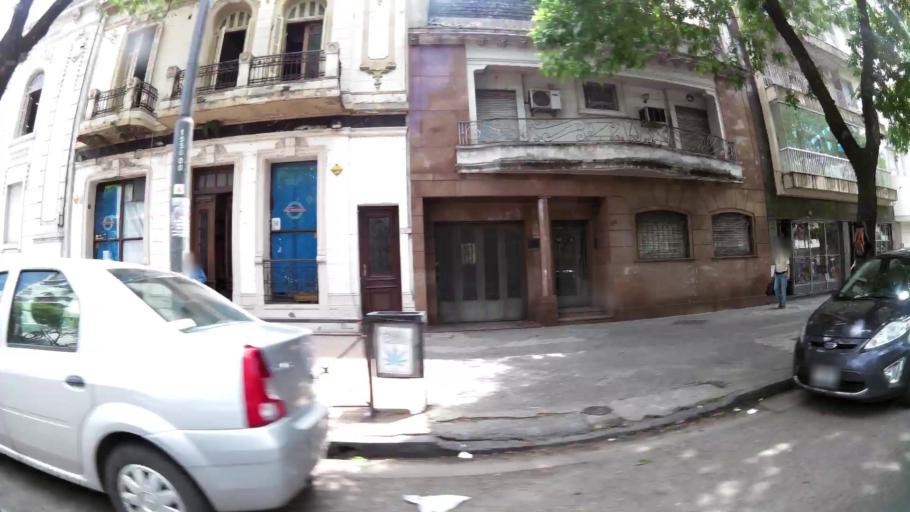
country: AR
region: Santa Fe
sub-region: Departamento de Rosario
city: Rosario
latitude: -32.9551
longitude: -60.6527
